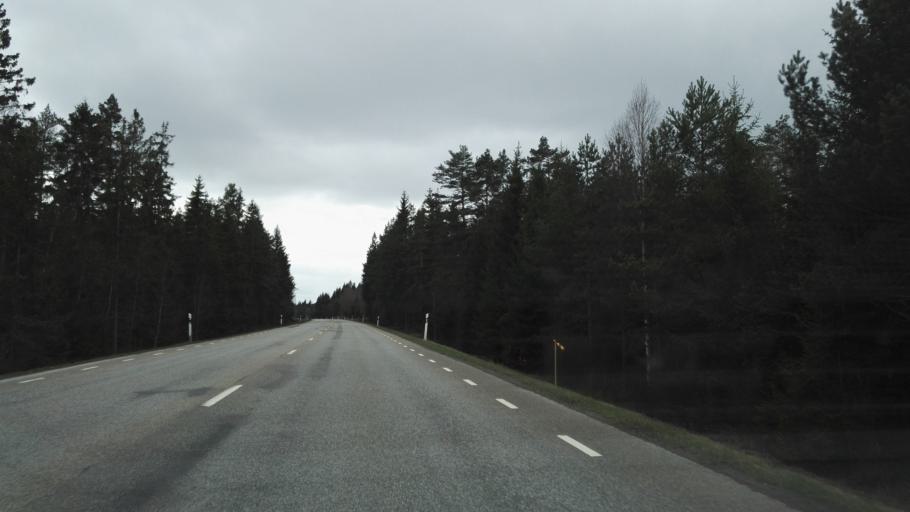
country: SE
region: Kronoberg
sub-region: Almhults Kommun
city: AElmhult
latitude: 56.6197
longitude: 14.2403
